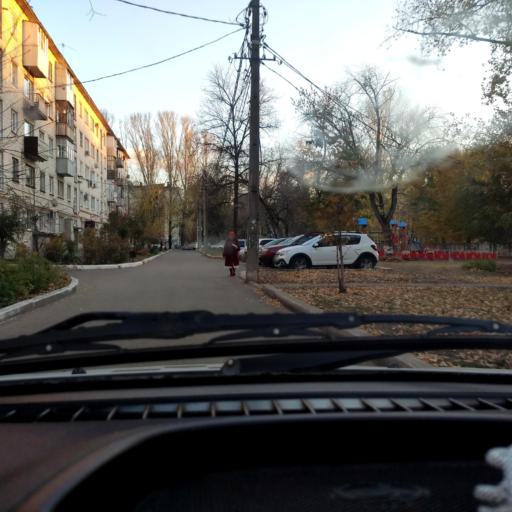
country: RU
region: Samara
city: Tol'yatti
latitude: 53.5029
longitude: 49.4080
